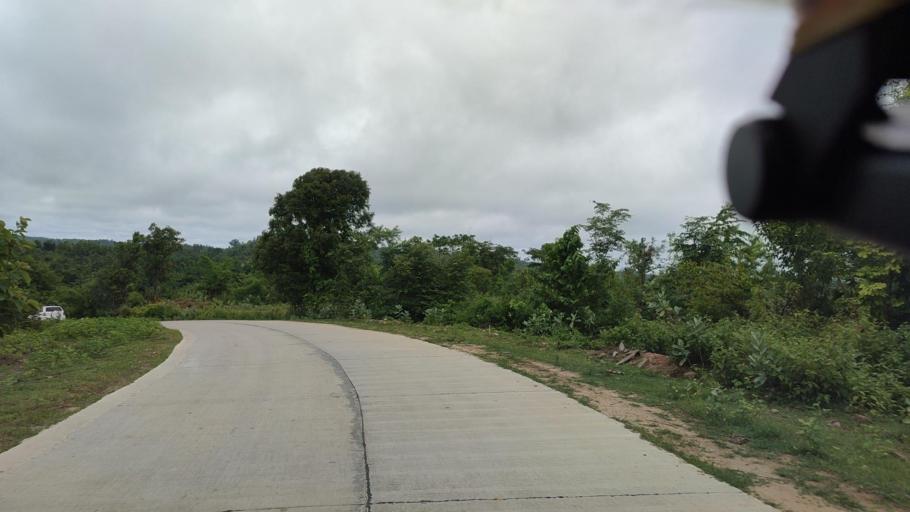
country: MM
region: Magway
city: Taungdwingyi
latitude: 20.0196
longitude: 95.8127
